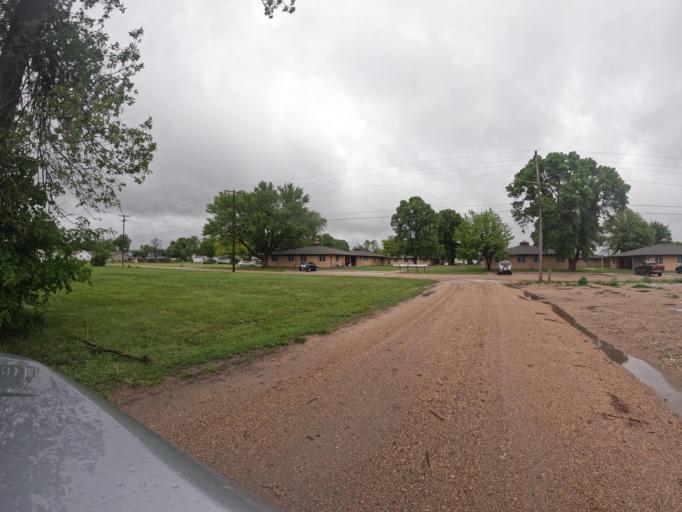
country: US
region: Nebraska
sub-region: Clay County
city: Harvard
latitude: 40.6178
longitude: -98.0917
